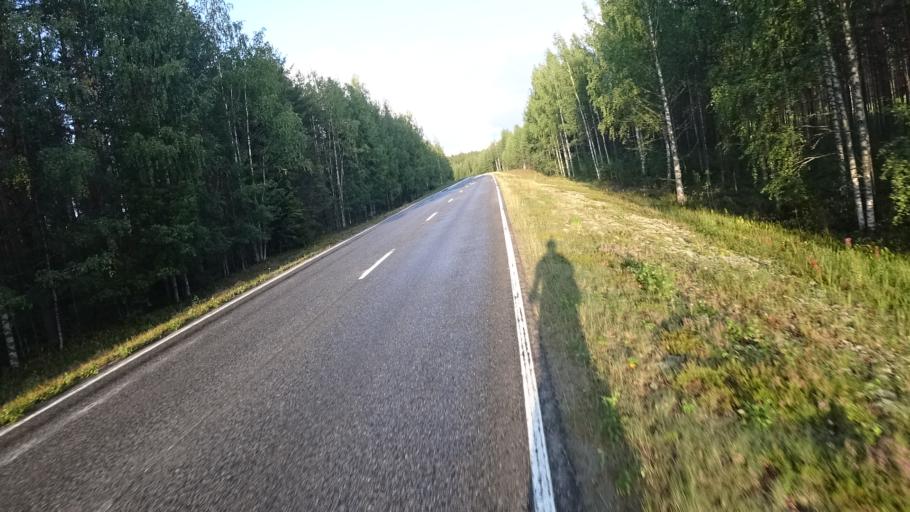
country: FI
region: North Karelia
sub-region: Joensuu
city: Ilomantsi
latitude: 62.6234
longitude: 31.1232
